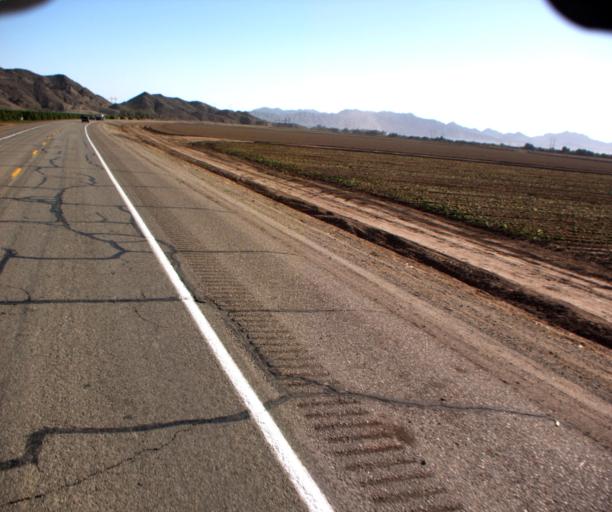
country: US
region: Arizona
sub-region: Yuma County
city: Fortuna Foothills
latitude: 32.7645
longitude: -114.4077
